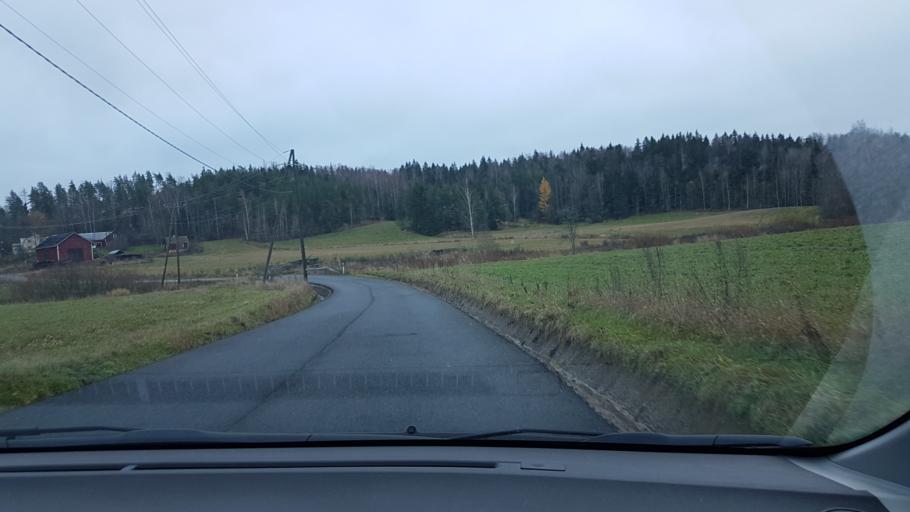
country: FI
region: Uusimaa
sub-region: Helsinki
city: Vantaa
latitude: 60.2824
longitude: 25.1430
